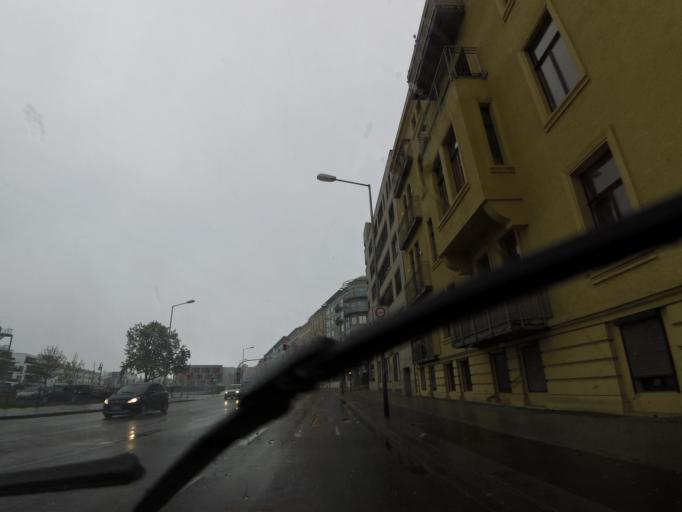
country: DE
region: Saxony-Anhalt
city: Magdeburg
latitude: 52.1216
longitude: 11.6337
